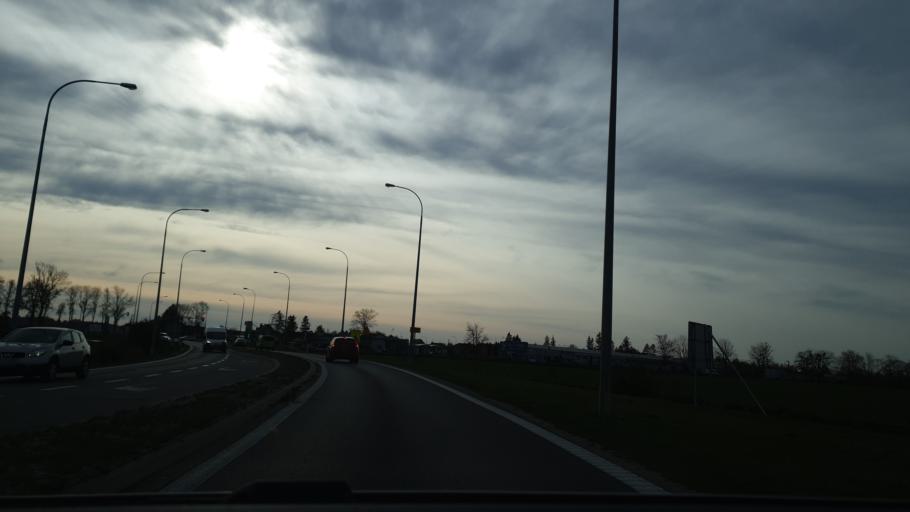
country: PL
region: Pomeranian Voivodeship
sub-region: Powiat pucki
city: Zelistrzewo
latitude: 54.6877
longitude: 18.3686
